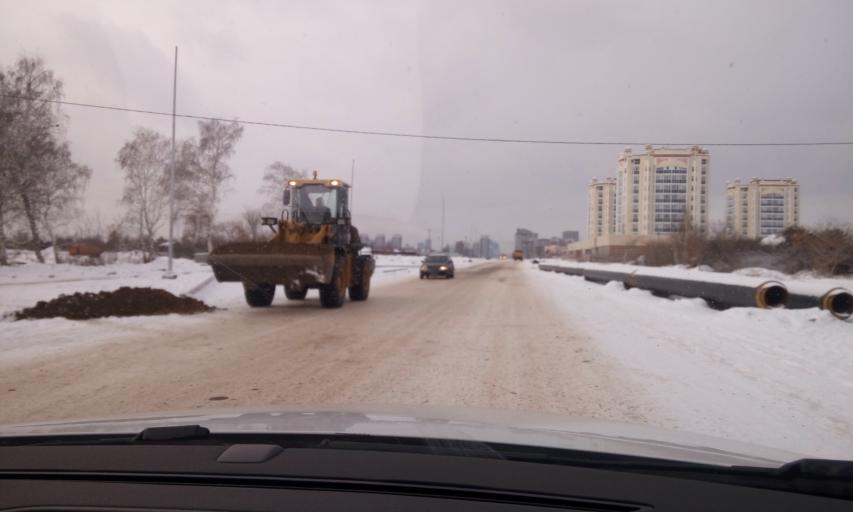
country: KZ
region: Astana Qalasy
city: Astana
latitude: 51.1185
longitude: 71.5083
